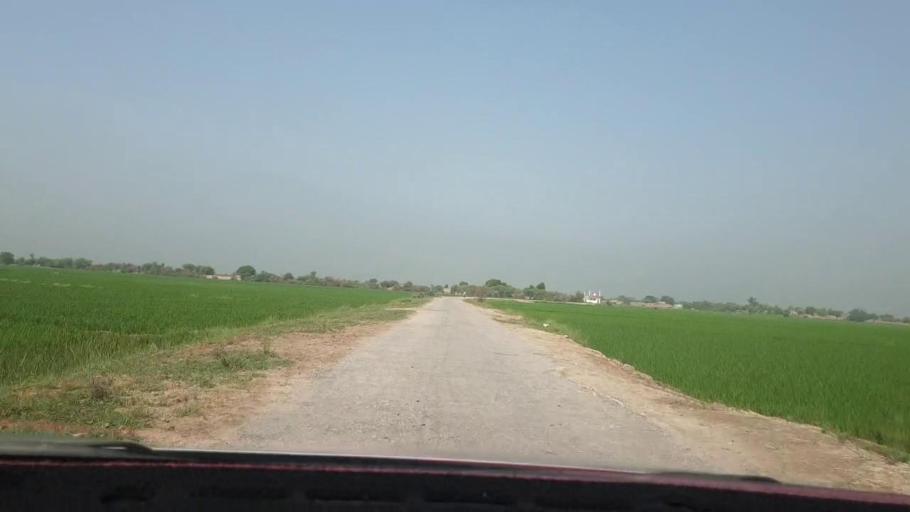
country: PK
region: Sindh
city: Nasirabad
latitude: 27.4312
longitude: 67.8964
